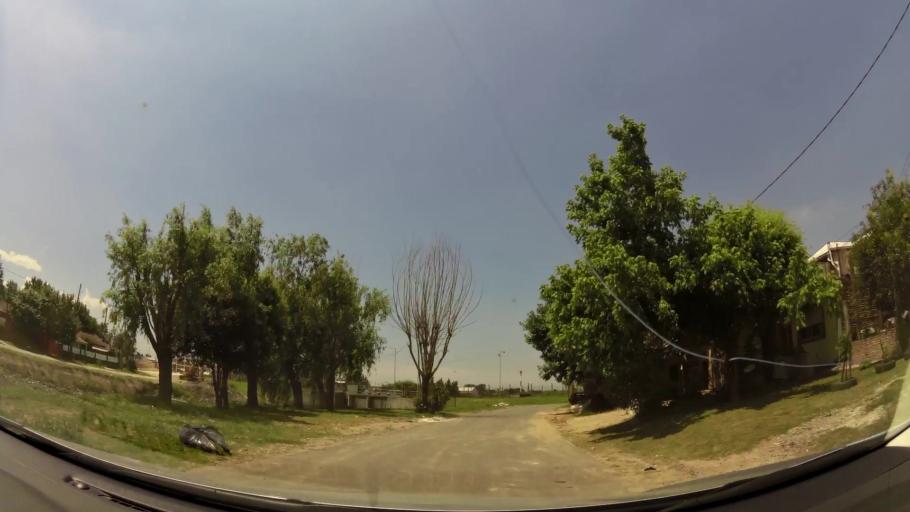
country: AR
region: Buenos Aires
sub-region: Partido de Tigre
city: Tigre
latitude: -34.4498
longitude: -58.5968
